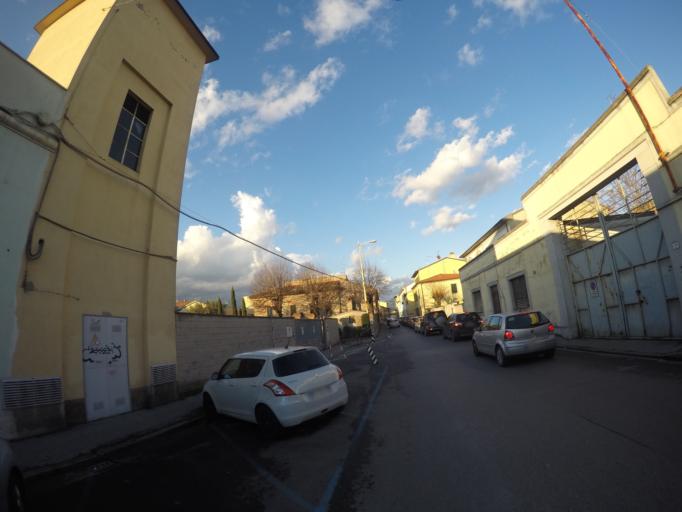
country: IT
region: Tuscany
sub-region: Provincia di Prato
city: Prato
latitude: 43.8809
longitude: 11.0895
